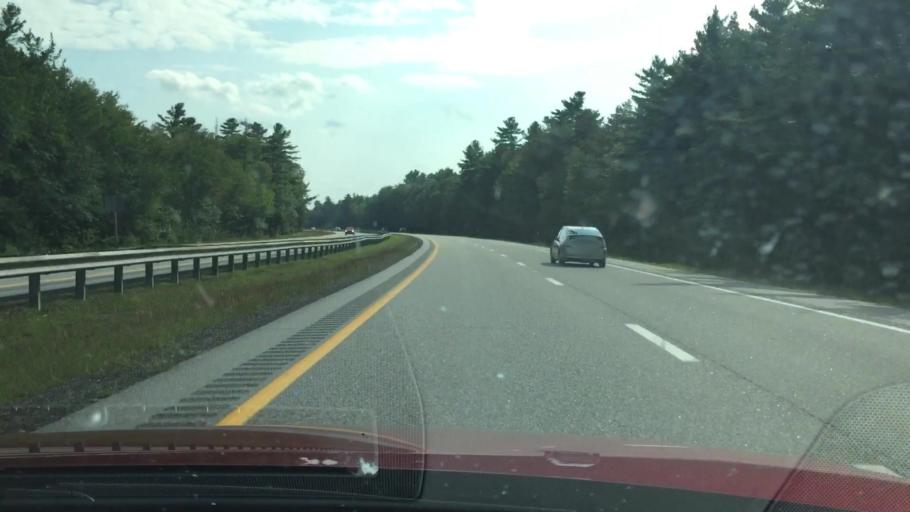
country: US
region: Maine
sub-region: Cumberland County
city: New Gloucester
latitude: 43.9722
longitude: -70.3221
